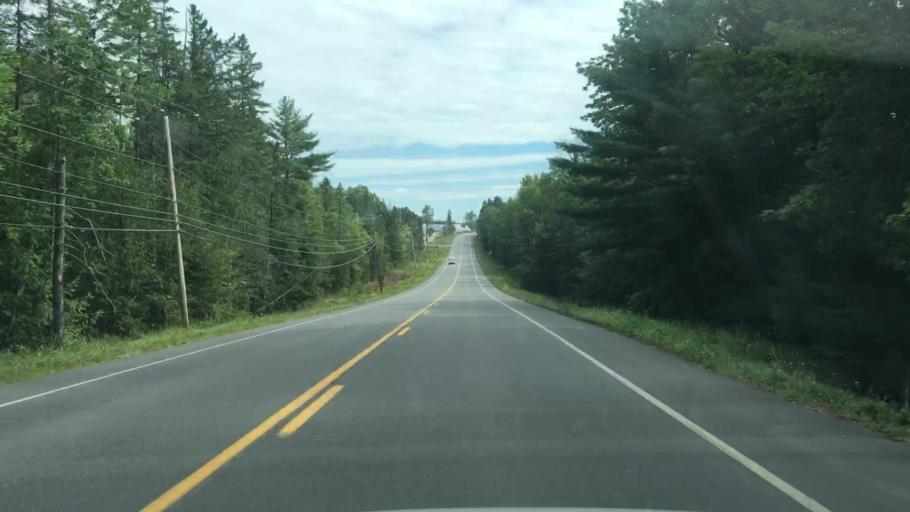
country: US
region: Maine
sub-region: Piscataquis County
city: Dover-Foxcroft
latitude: 45.1991
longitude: -69.2034
